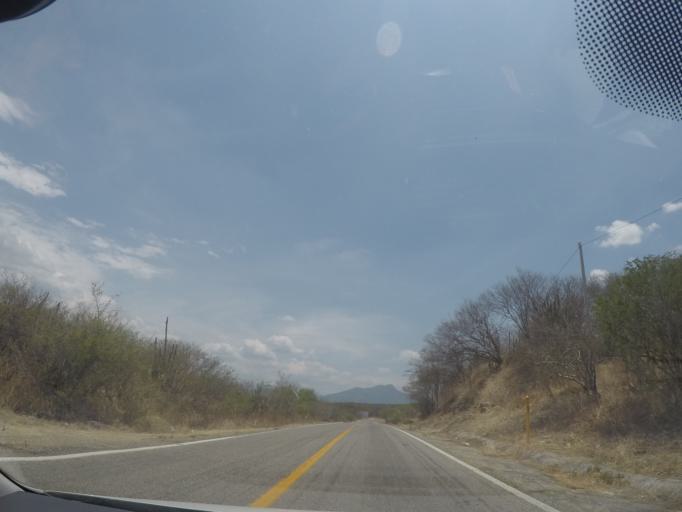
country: MX
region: Oaxaca
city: Magdalena Tequisistlan
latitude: 16.4094
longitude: -95.6279
